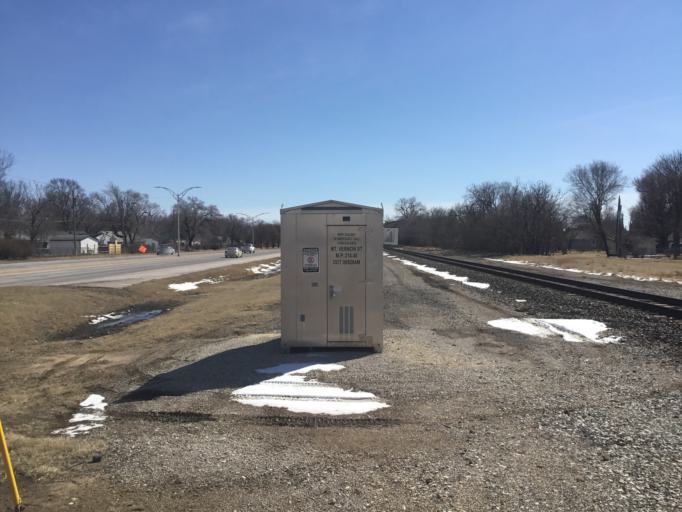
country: US
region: Kansas
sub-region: Sedgwick County
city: Wichita
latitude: 37.6571
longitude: -97.3200
